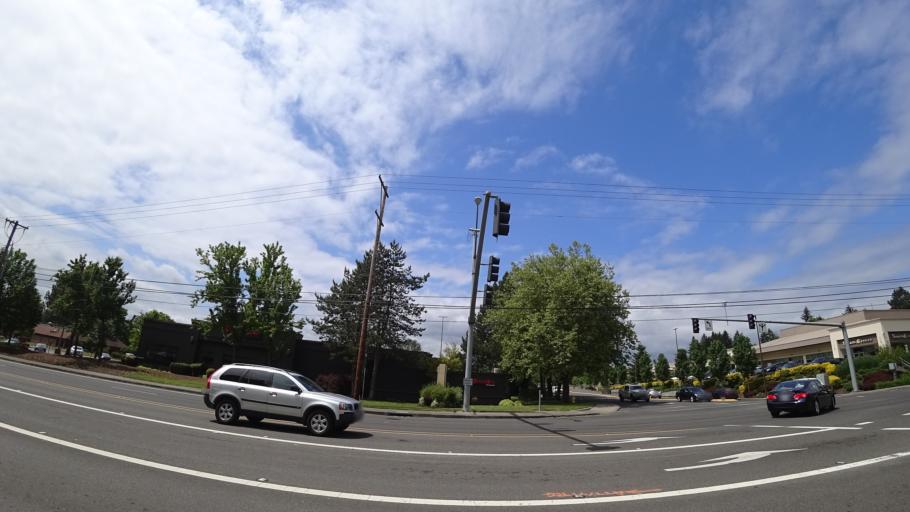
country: US
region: Oregon
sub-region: Washington County
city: Tigard
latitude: 45.4456
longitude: -122.7764
